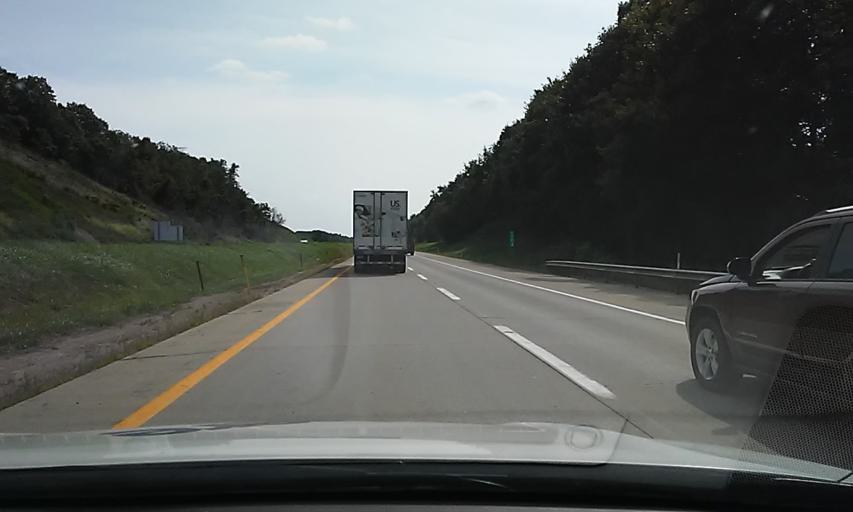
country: US
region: Pennsylvania
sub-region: Westmoreland County
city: Delmont
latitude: 40.3610
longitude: -79.5588
